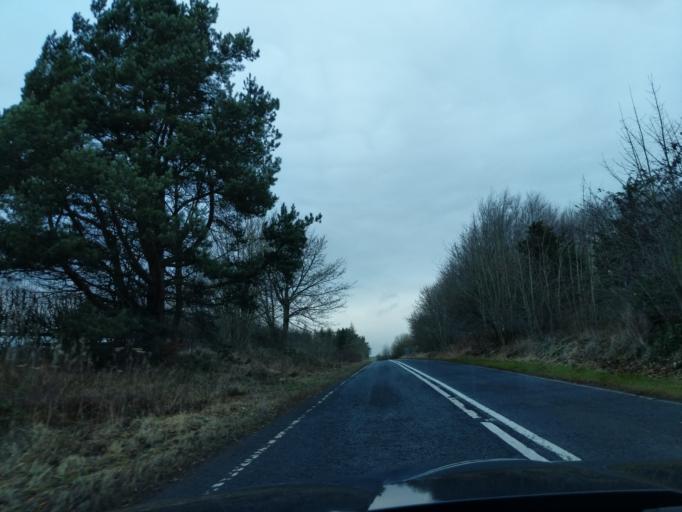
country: GB
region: England
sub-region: Northumberland
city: Rothley
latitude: 55.1439
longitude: -1.9916
